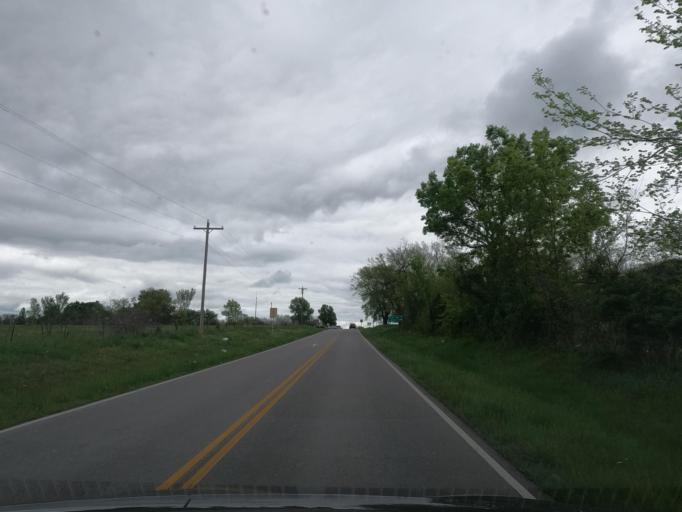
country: US
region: Missouri
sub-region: Jasper County
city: Oronogo
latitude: 37.3308
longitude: -94.4865
